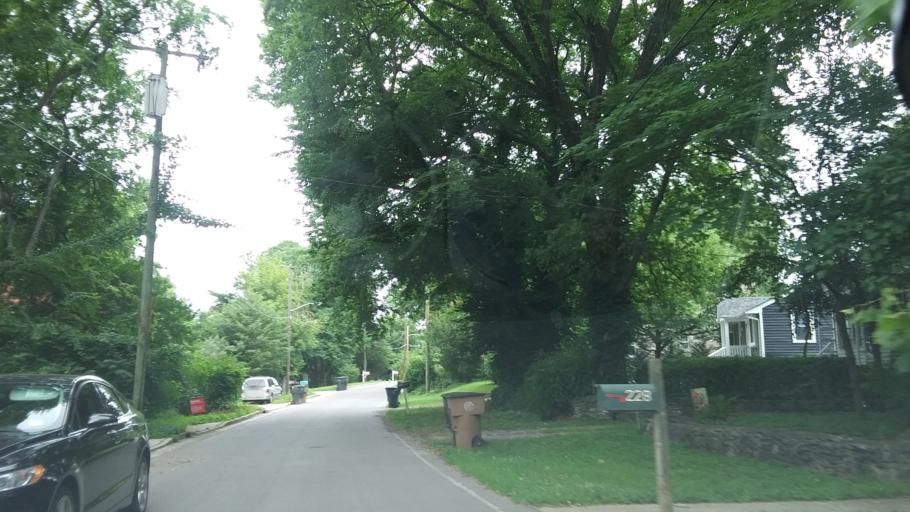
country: US
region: Tennessee
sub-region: Davidson County
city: Belle Meade
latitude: 36.1471
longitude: -86.8524
